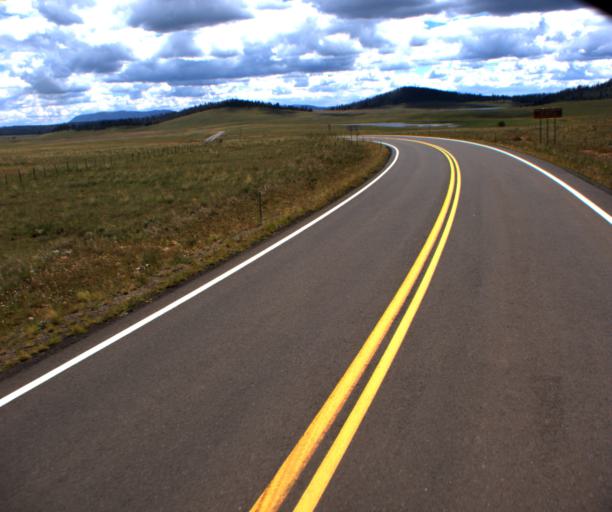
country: US
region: Arizona
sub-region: Apache County
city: Eagar
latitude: 33.9209
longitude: -109.4477
